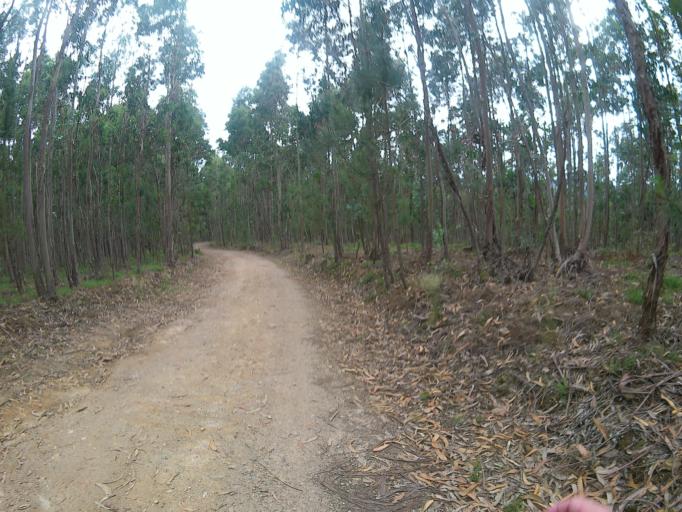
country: PT
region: Aveiro
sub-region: Albergaria-A-Velha
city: Branca
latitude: 40.7635
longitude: -8.4312
